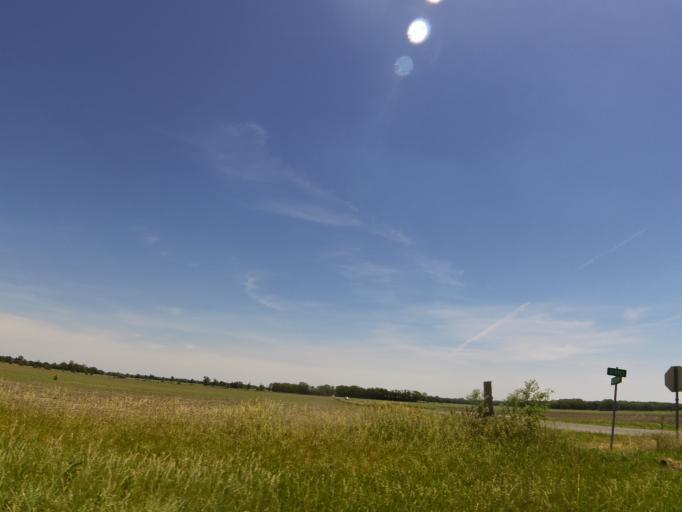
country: US
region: Illinois
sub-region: Vermilion County
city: Hoopeston
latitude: 40.4443
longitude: -87.6866
